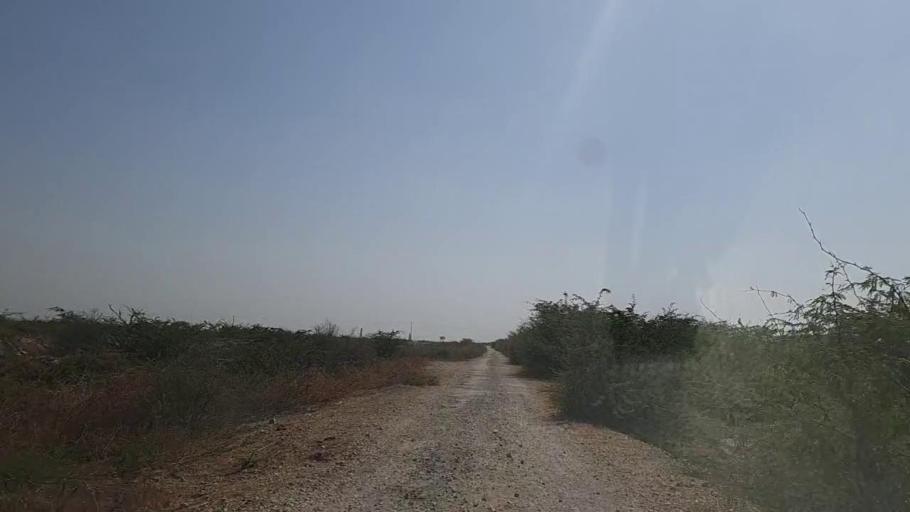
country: PK
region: Sindh
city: Naukot
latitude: 24.6268
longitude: 69.2707
